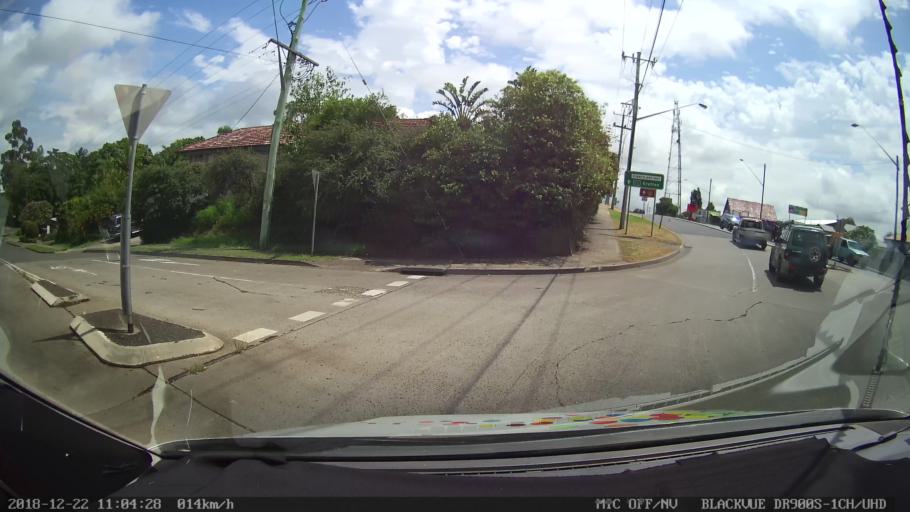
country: AU
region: New South Wales
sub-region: Clarence Valley
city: South Grafton
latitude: -29.7037
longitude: 152.9402
